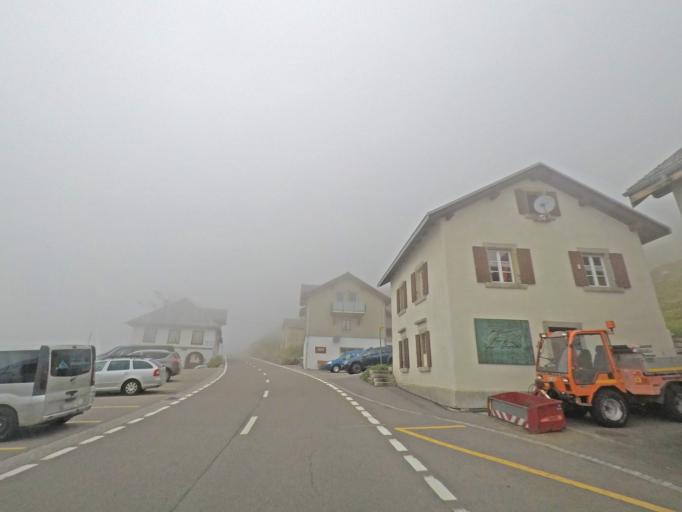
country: CH
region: Uri
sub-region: Uri
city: Andermatt
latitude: 46.5929
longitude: 8.4614
